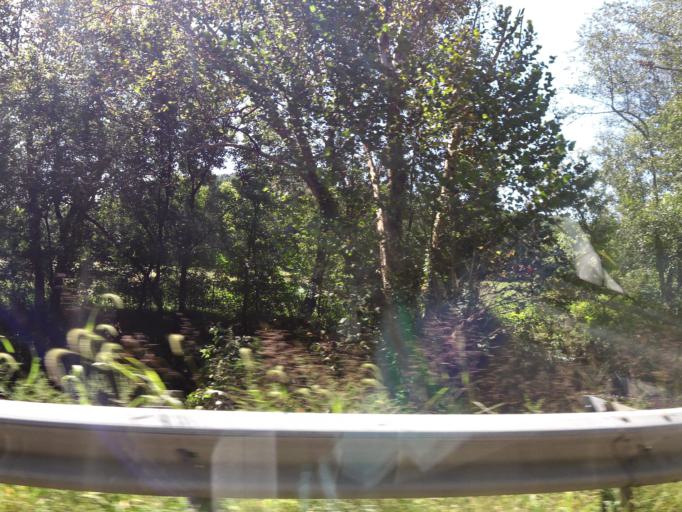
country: US
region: Kentucky
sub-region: Clay County
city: Manchester
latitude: 37.0896
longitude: -83.6994
